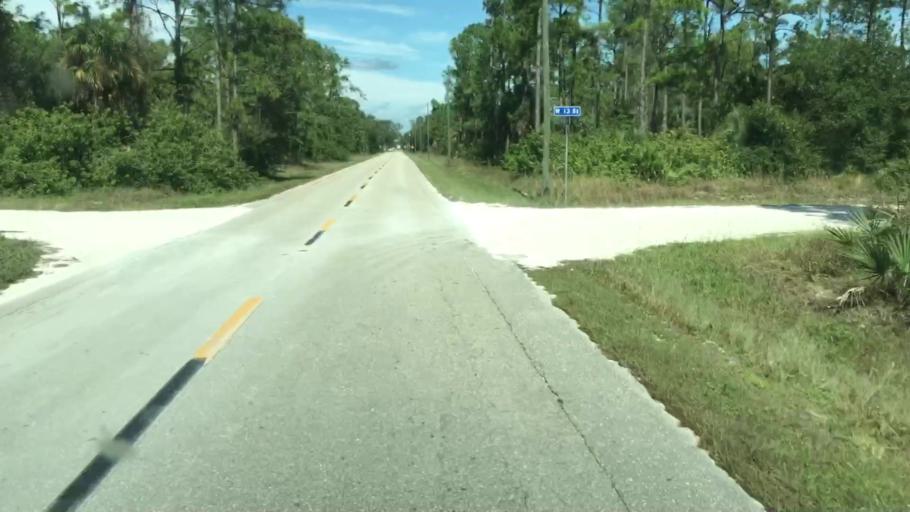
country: US
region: Florida
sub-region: Lee County
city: Lehigh Acres
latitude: 26.6470
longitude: -81.6465
